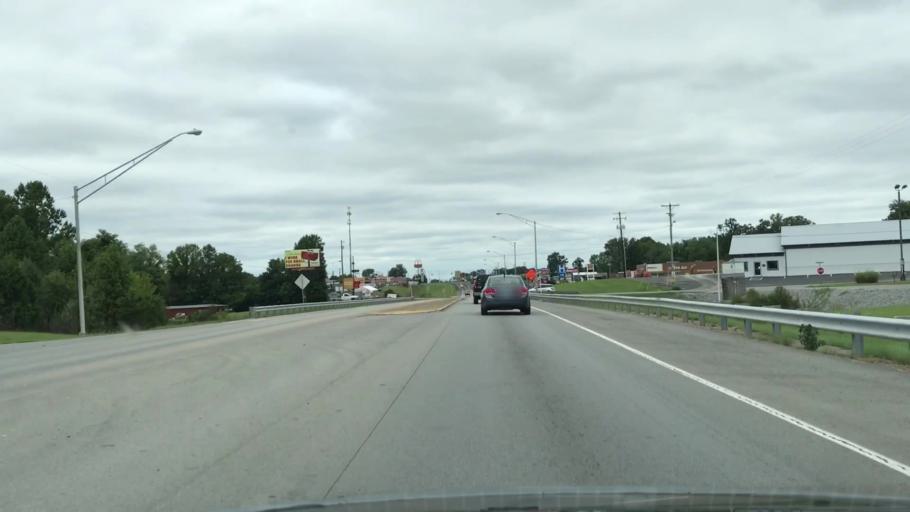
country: US
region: Kentucky
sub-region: Russell County
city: Russell Springs
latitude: 37.0566
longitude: -85.0704
